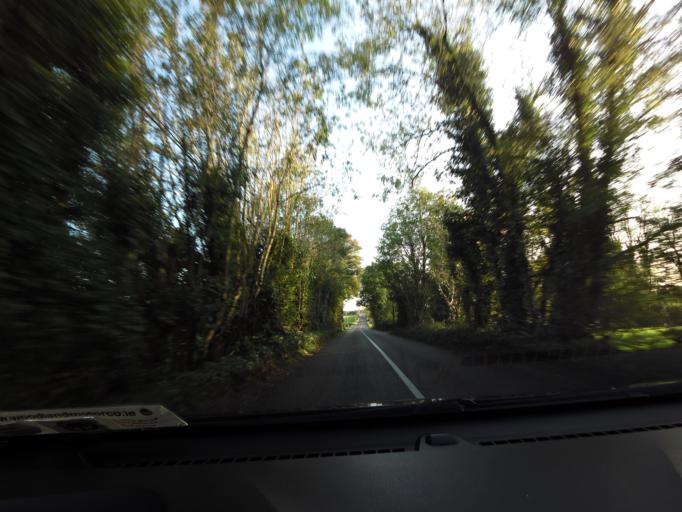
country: IE
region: Connaught
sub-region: Roscommon
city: Castlerea
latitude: 53.7106
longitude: -8.5641
